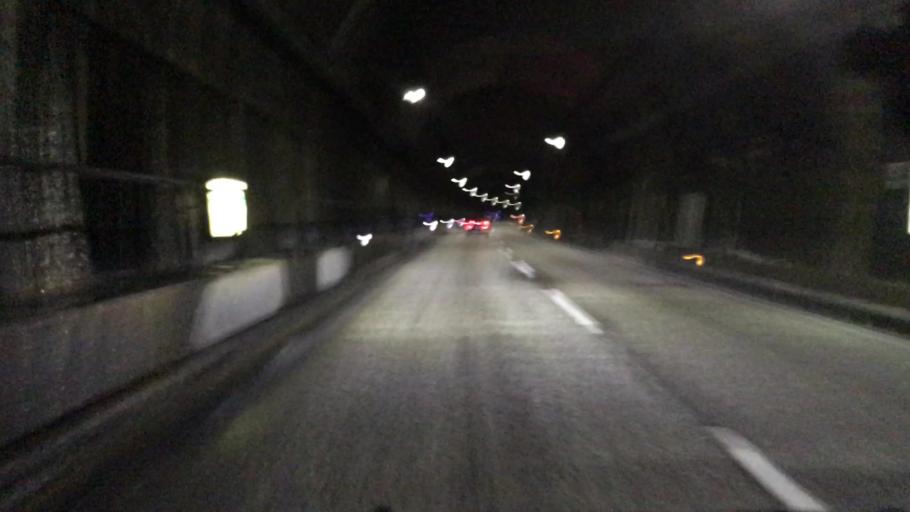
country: JP
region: Hyogo
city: Kobe
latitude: 34.7414
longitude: 135.1720
